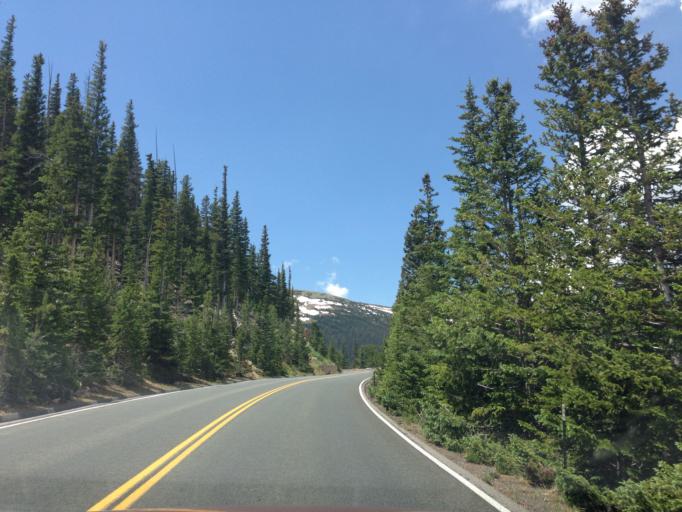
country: US
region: Colorado
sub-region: Larimer County
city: Estes Park
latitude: 40.3907
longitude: -105.6501
